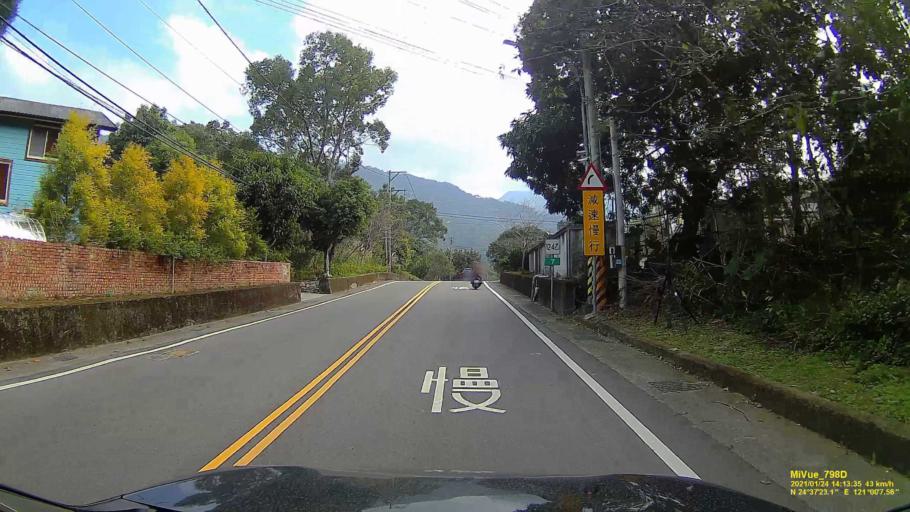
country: TW
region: Taiwan
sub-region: Hsinchu
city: Hsinchu
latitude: 24.6227
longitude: 121.0023
